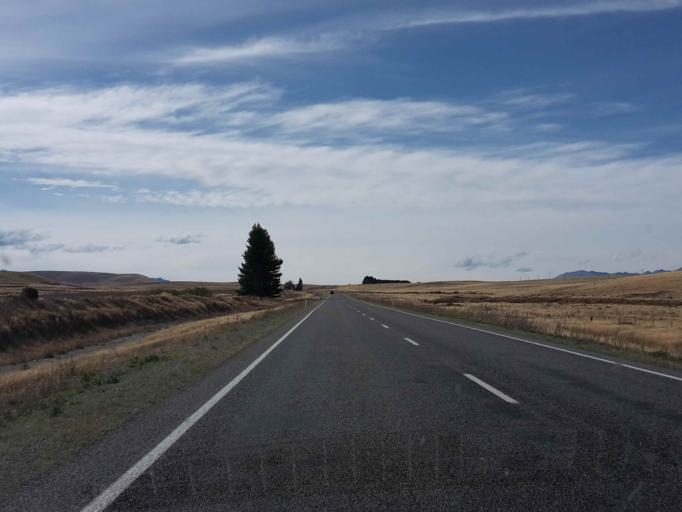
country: NZ
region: Canterbury
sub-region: Timaru District
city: Pleasant Point
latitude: -44.0485
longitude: 170.3764
